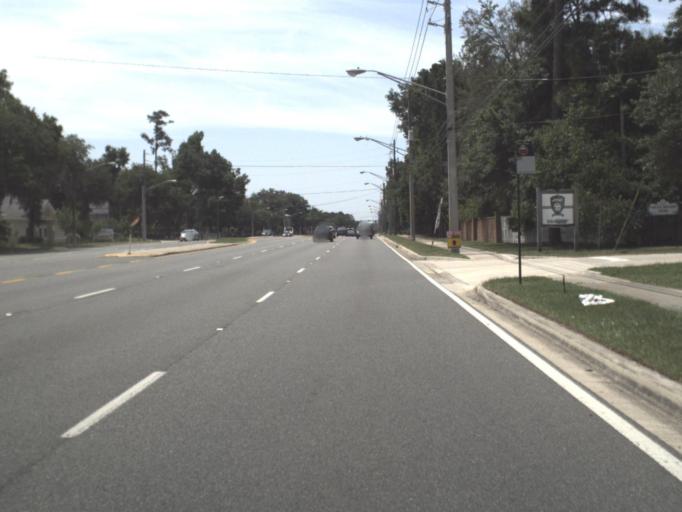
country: US
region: Florida
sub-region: Saint Johns County
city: Fruit Cove
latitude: 30.1540
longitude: -81.6328
